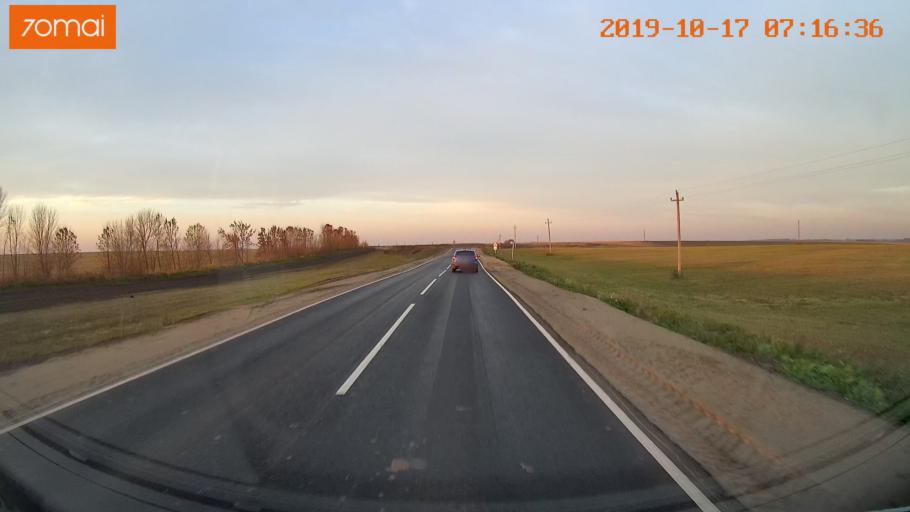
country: RU
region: Vladimir
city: Suzdal'
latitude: 56.3712
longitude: 40.2458
